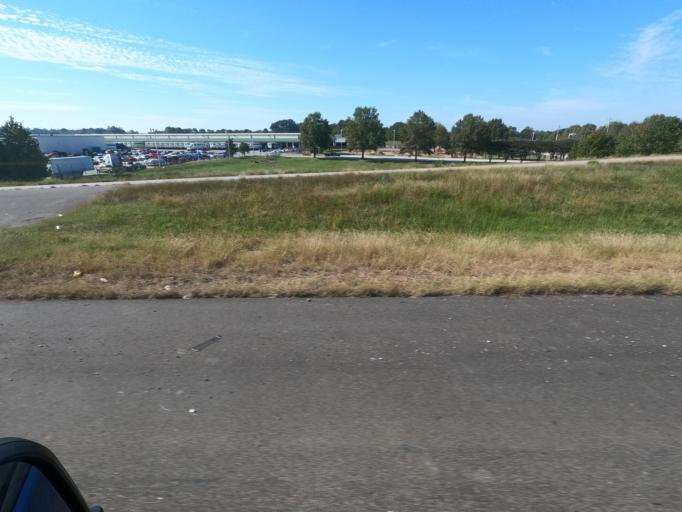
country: US
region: Tennessee
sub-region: Shelby County
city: Arlington
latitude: 35.2856
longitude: -89.6833
